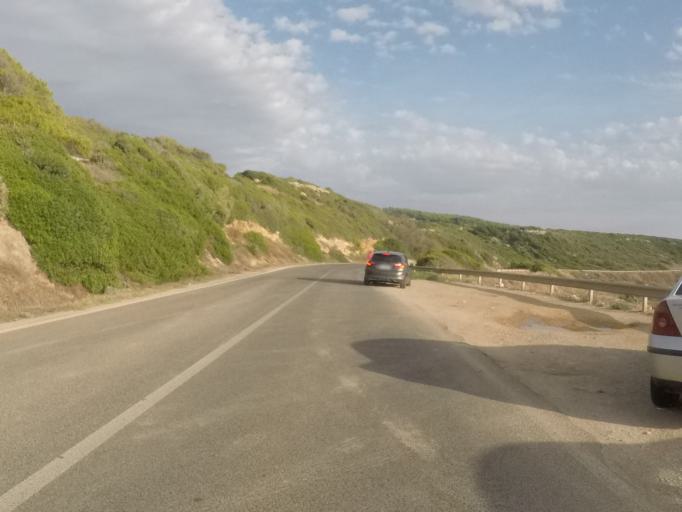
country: IT
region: Sardinia
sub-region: Provincia di Sassari
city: Alghero
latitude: 40.5414
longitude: 8.3224
